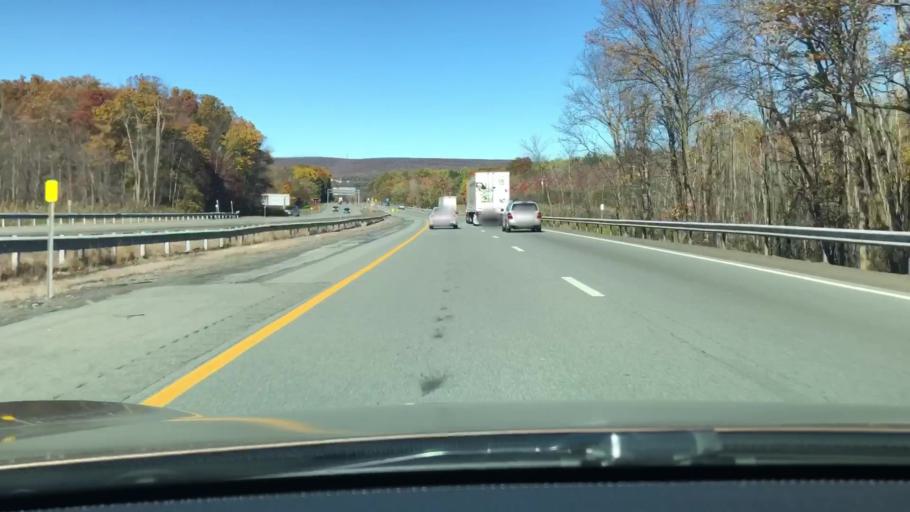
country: US
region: New York
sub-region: Orange County
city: Central Valley
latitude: 41.3290
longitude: -74.1129
